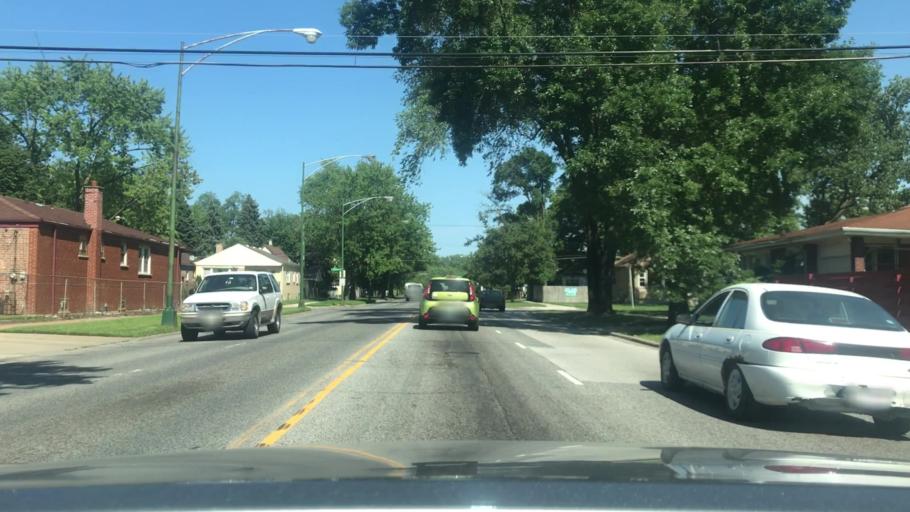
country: US
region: Illinois
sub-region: Cook County
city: Burnham
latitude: 41.7081
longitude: -87.5628
